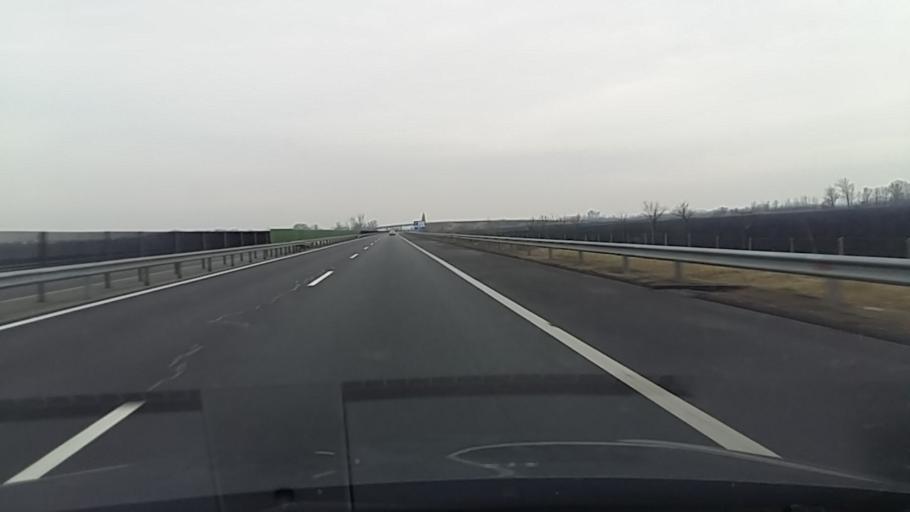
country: HU
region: Hajdu-Bihar
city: Gorbehaza
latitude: 47.8346
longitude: 21.3336
